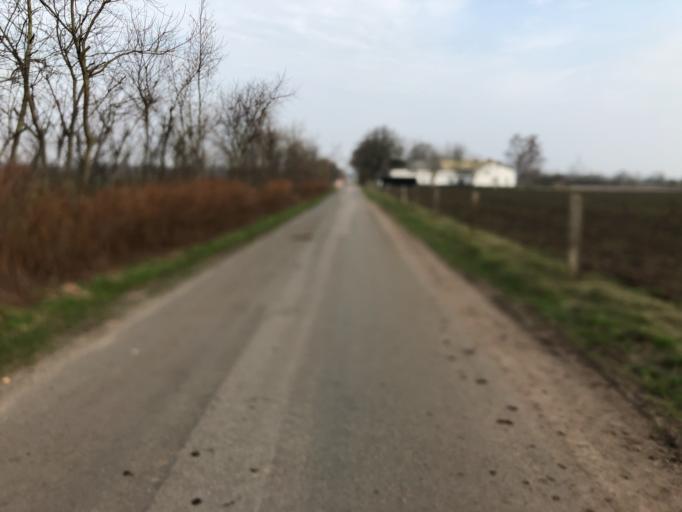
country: DE
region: Schleswig-Holstein
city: Wanderup
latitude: 54.6951
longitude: 9.3652
